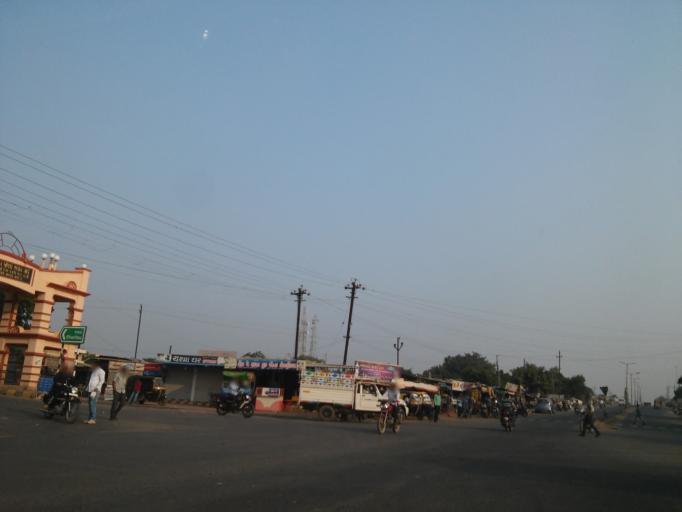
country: IN
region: Gujarat
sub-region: Kachchh
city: Bhachau
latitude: 23.2934
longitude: 70.3481
